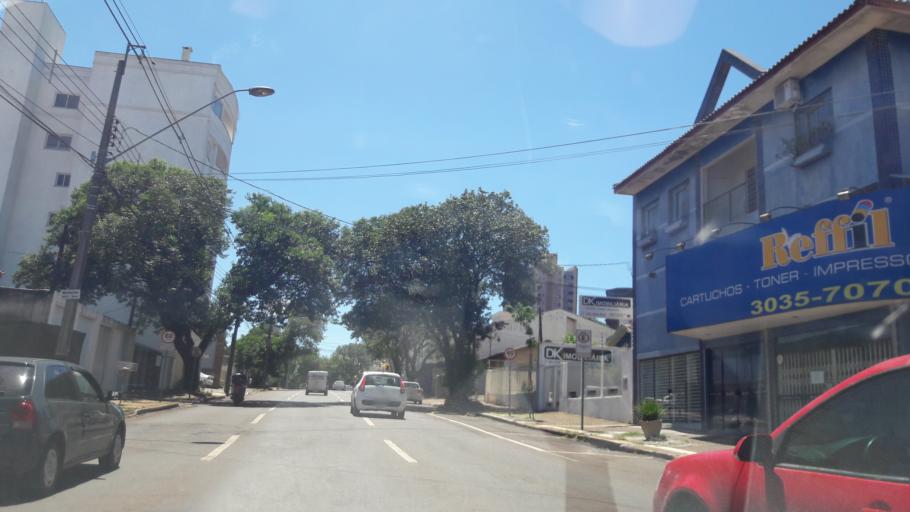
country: BR
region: Parana
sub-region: Cascavel
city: Cascavel
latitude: -24.9519
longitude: -53.4641
